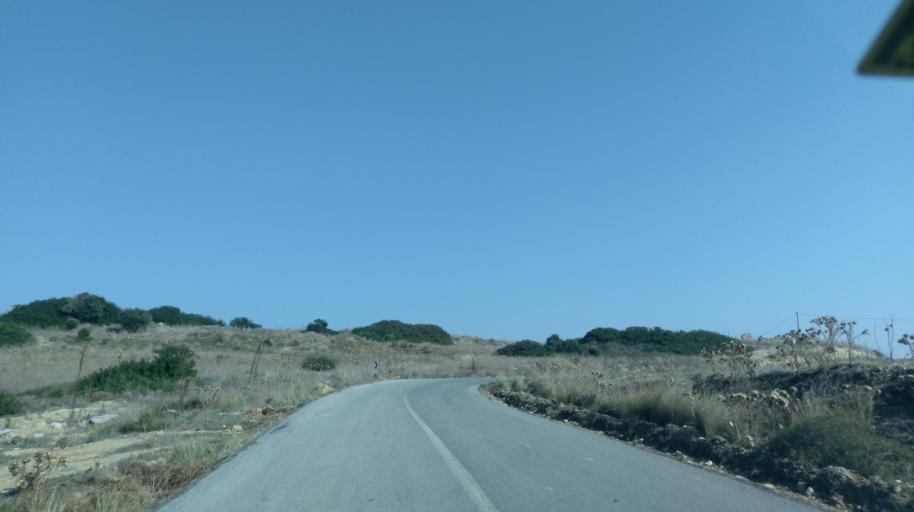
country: CY
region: Ammochostos
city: Leonarisso
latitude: 35.5066
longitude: 34.2452
